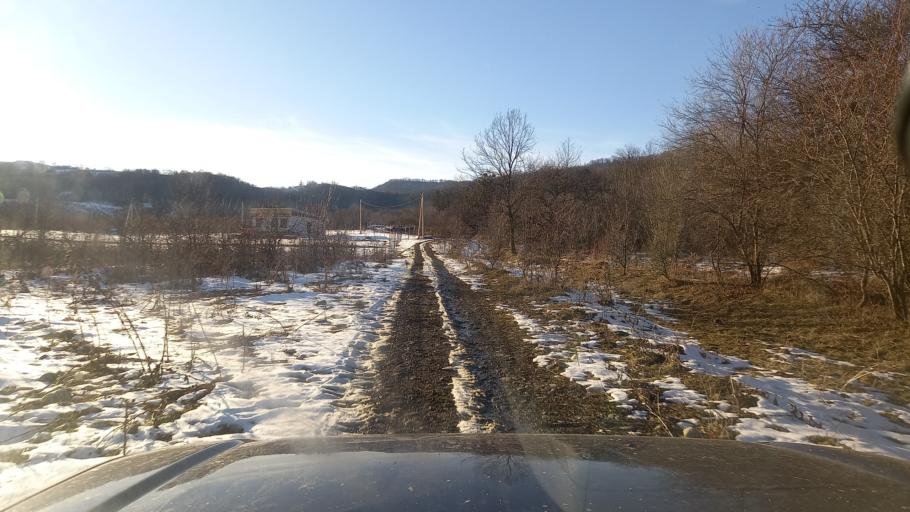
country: RU
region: Adygeya
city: Kamennomostskiy
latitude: 44.2288
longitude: 40.1700
